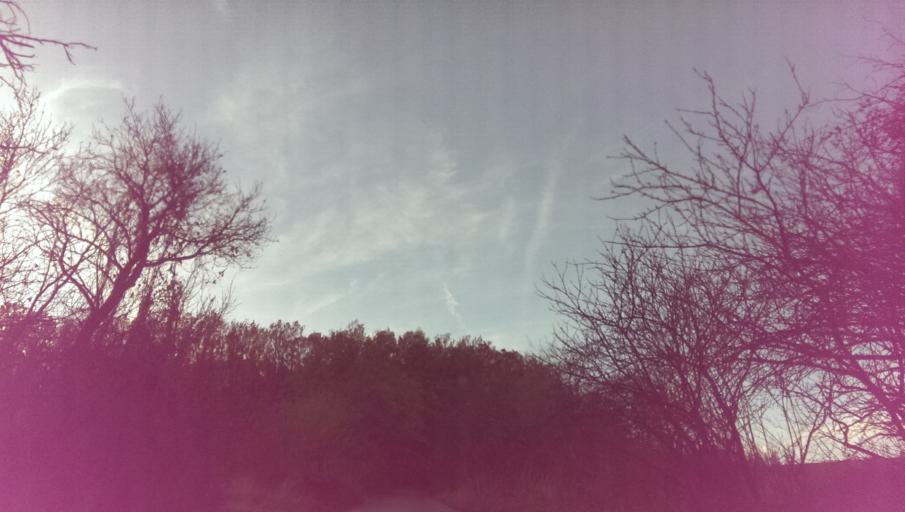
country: CZ
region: Zlin
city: Brezolupy
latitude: 49.1427
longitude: 17.6009
